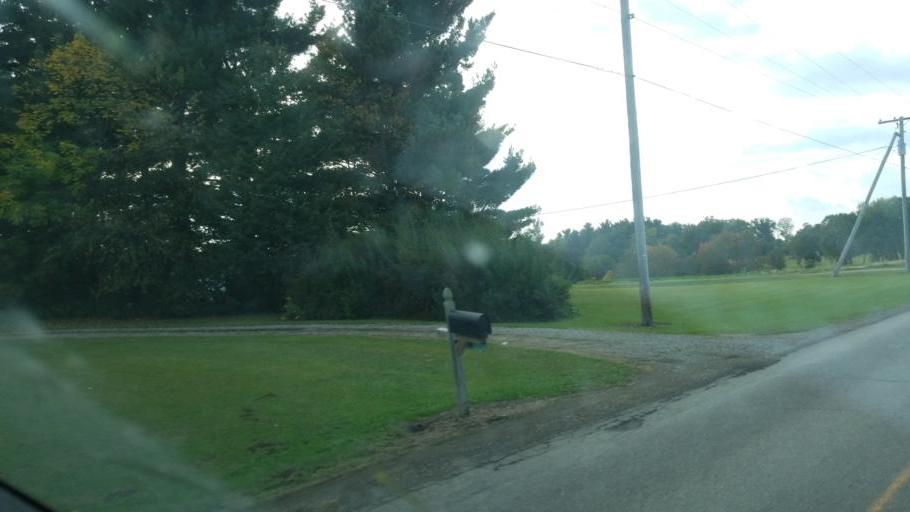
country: US
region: Ohio
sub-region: Knox County
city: Danville
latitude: 40.4529
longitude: -82.2757
